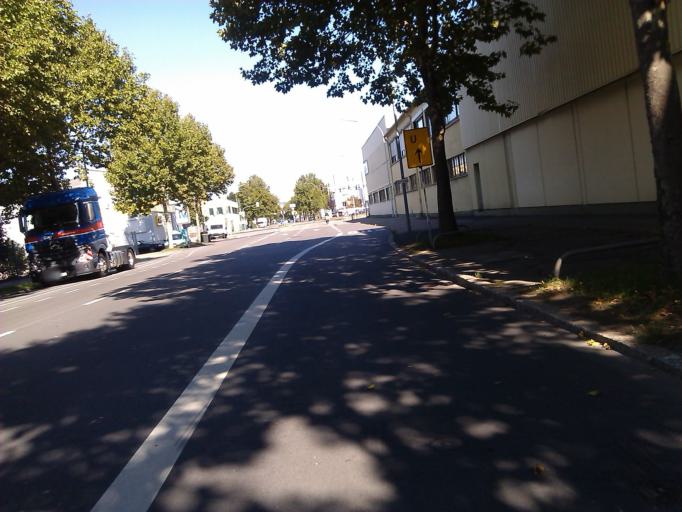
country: DE
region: Baden-Wuerttemberg
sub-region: Regierungsbezirk Stuttgart
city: Neckarsulm
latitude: 49.1678
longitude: 9.2192
